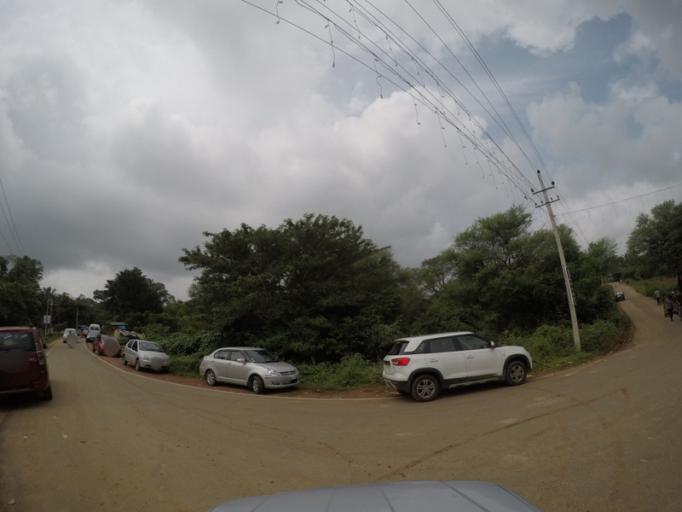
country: IN
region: Karnataka
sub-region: Bangalore Rural
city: Nelamangala
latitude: 13.1430
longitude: 77.4836
